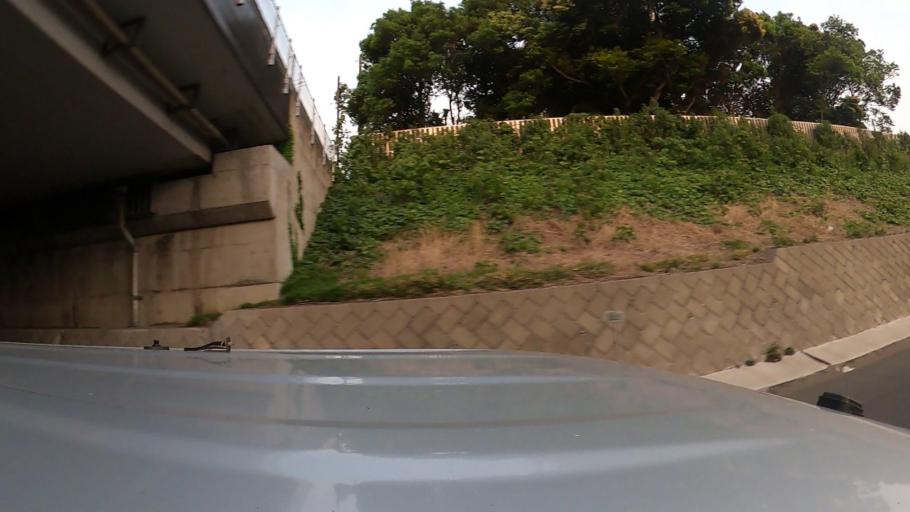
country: JP
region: Ibaraki
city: Moriya
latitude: 35.9662
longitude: 139.9793
